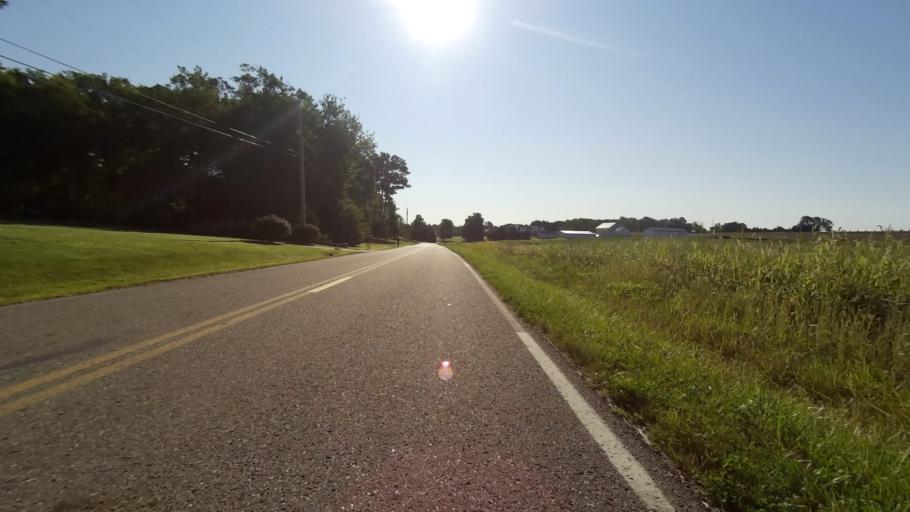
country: US
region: Ohio
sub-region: Portage County
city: Mantua
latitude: 41.2931
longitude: -81.2709
